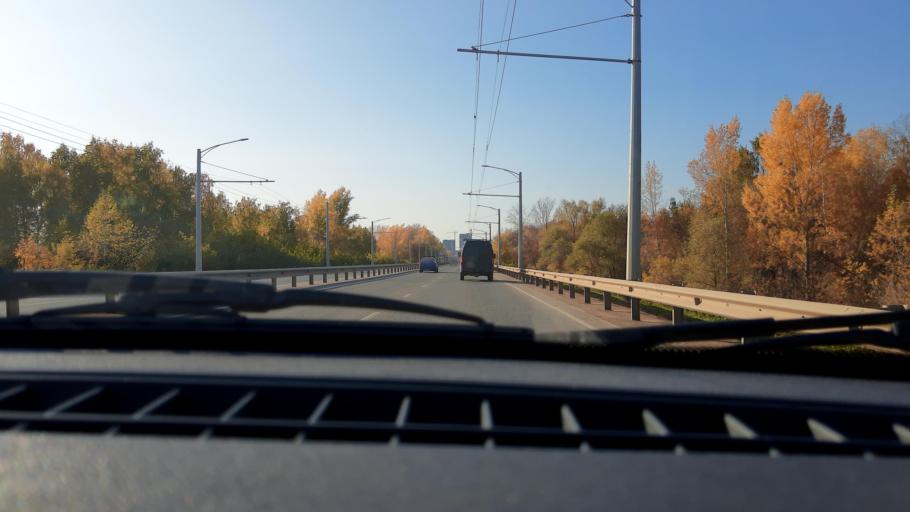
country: RU
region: Bashkortostan
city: Ufa
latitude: 54.7669
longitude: 55.9332
